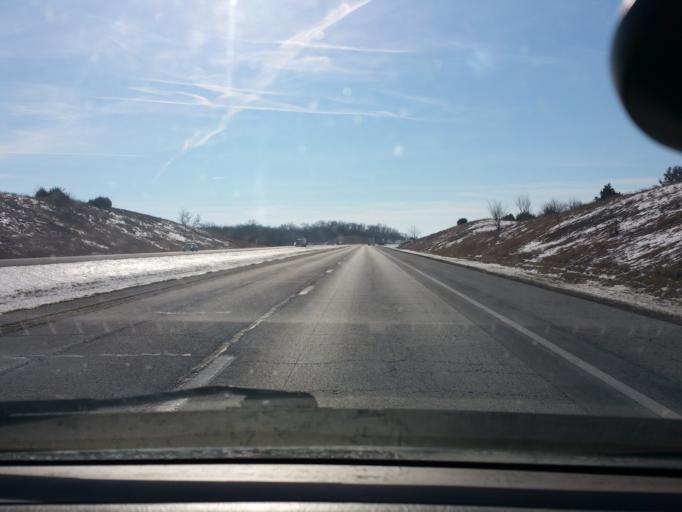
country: US
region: Missouri
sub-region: Harrison County
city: Bethany
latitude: 40.1859
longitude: -94.0149
